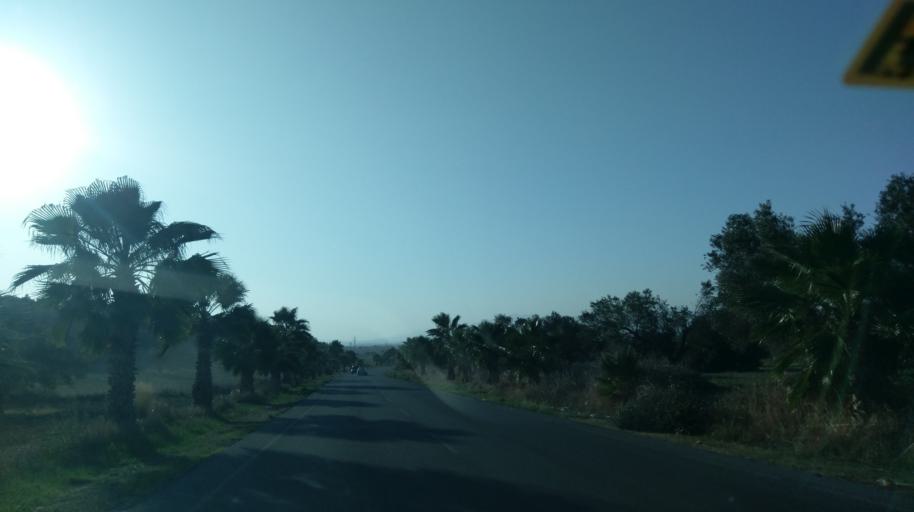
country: CY
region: Ammochostos
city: Leonarisso
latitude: 35.3784
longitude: 34.0564
